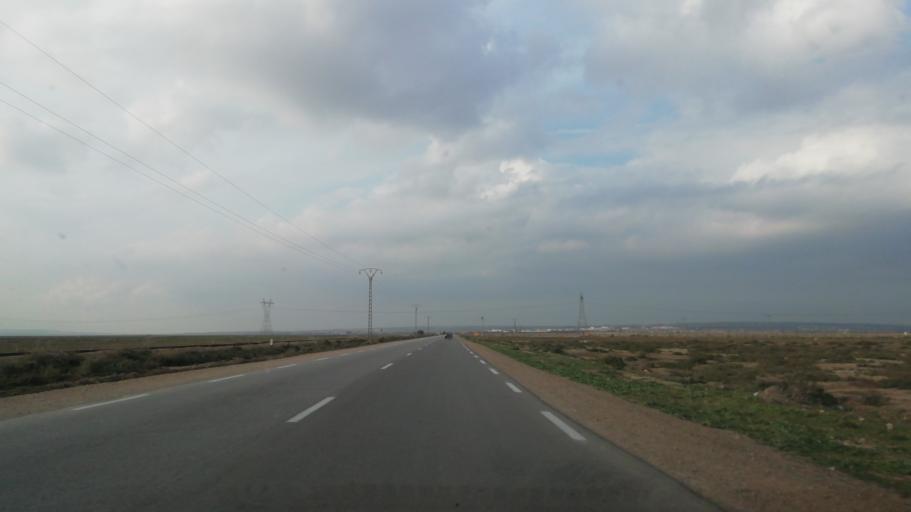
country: DZ
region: Mascara
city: Sig
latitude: 35.6994
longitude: -0.0243
